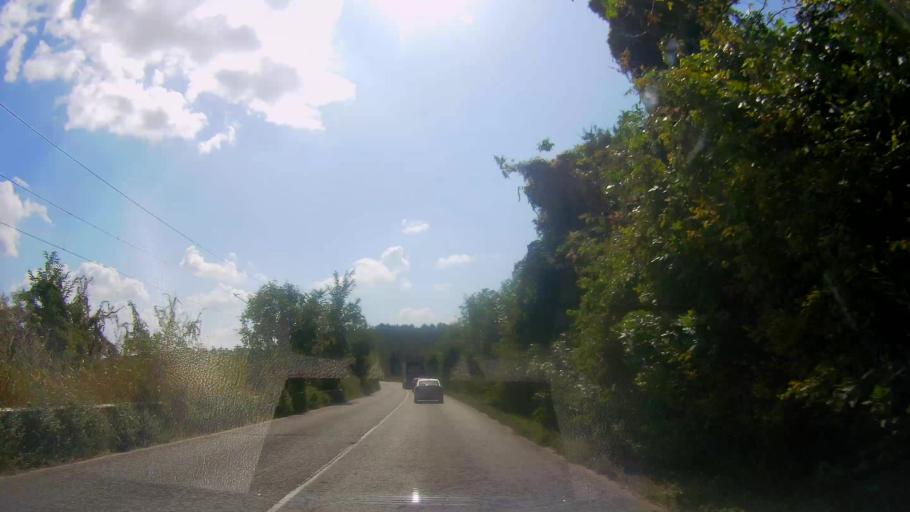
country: BG
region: Veliko Turnovo
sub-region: Obshtina Polski Trumbesh
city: Polski Trumbesh
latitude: 43.4351
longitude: 25.6553
